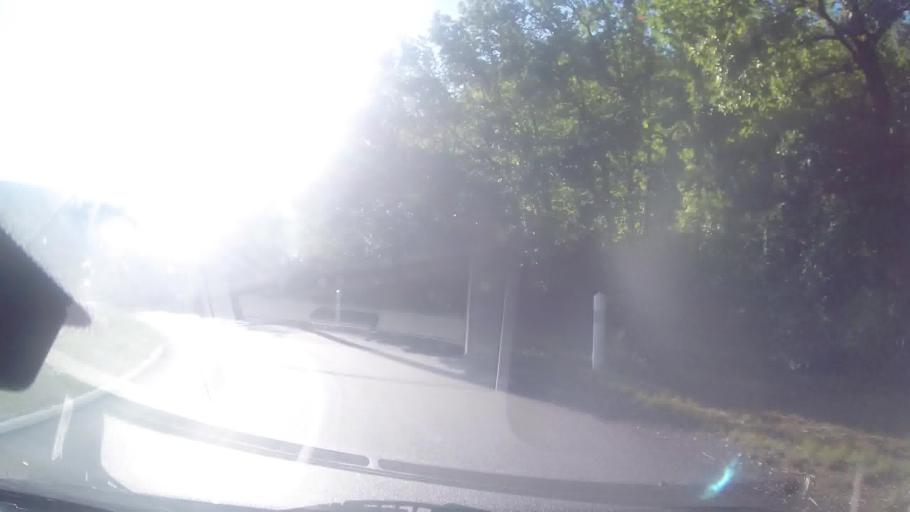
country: FR
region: Aquitaine
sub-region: Departement de la Dordogne
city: Cenac-et-Saint-Julien
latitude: 44.7891
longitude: 1.1772
